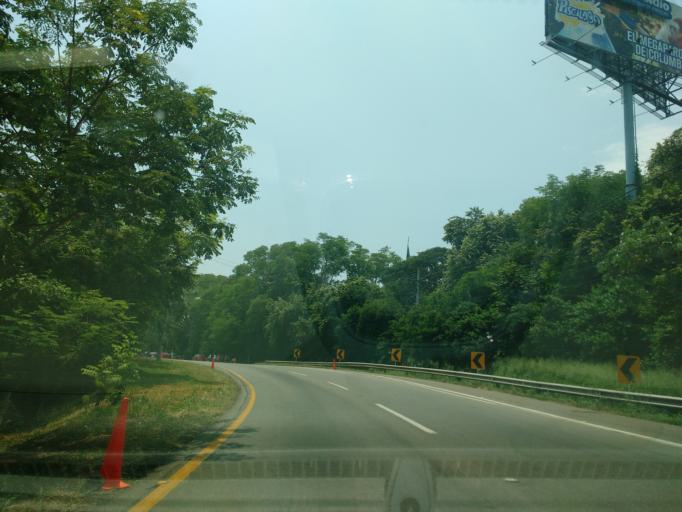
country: CO
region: Tolima
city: Melgar
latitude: 4.2157
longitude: -74.6848
